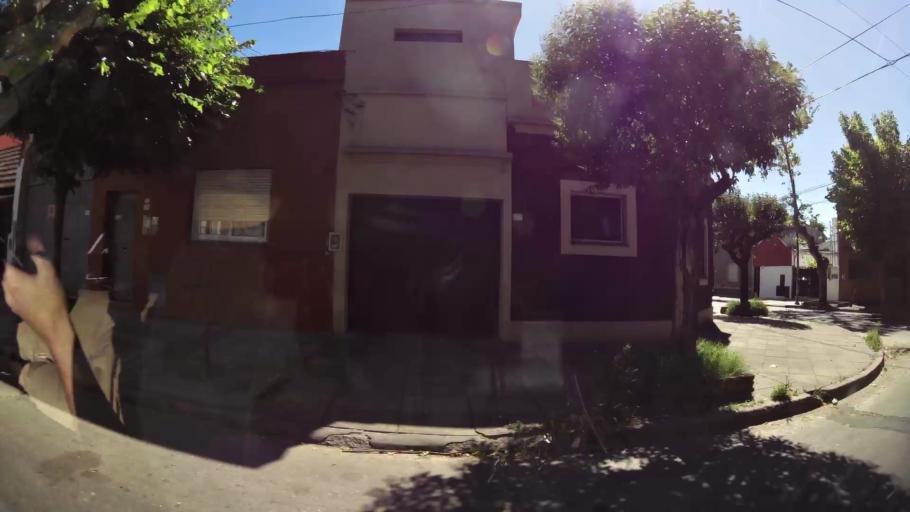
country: AR
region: Buenos Aires
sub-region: Partido de General San Martin
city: General San Martin
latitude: -34.5685
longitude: -58.5348
